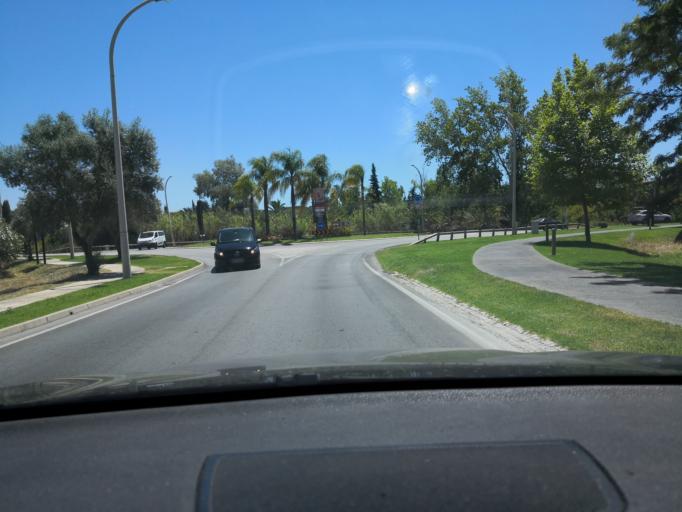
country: PT
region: Faro
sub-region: Loule
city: Vilamoura
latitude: 37.1030
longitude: -8.1248
